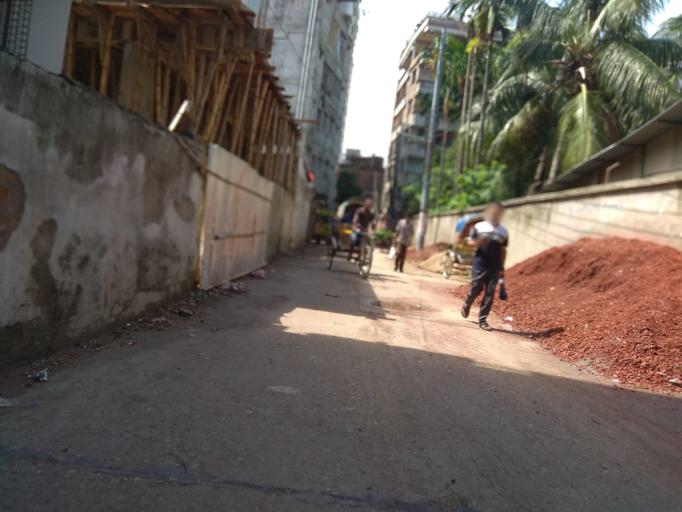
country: BD
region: Dhaka
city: Azimpur
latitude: 23.7996
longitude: 90.3576
